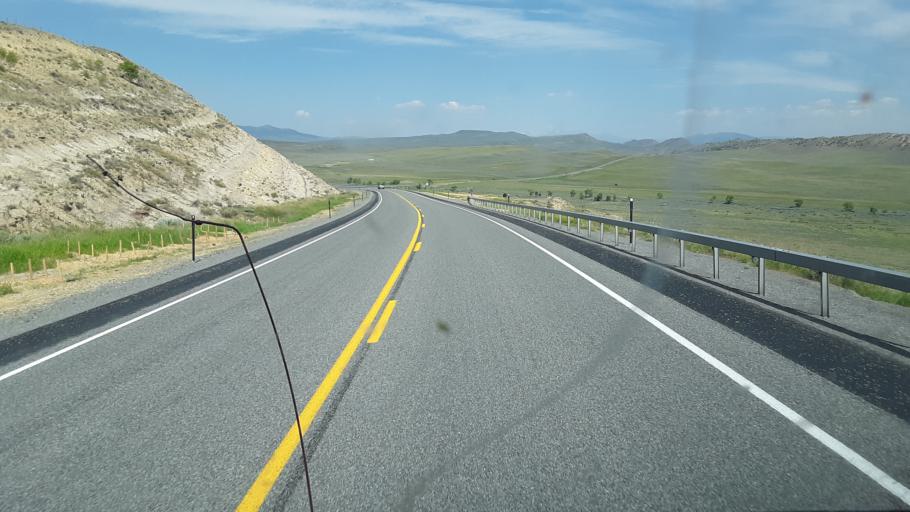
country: US
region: Wyoming
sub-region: Park County
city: Cody
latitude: 44.2723
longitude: -108.8766
